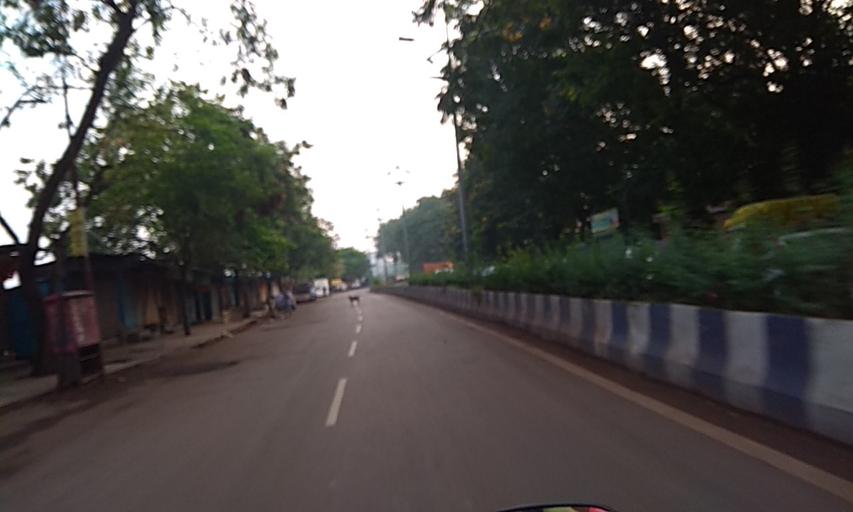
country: IN
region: Maharashtra
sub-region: Pune Division
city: Pune
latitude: 18.5225
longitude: 73.8564
